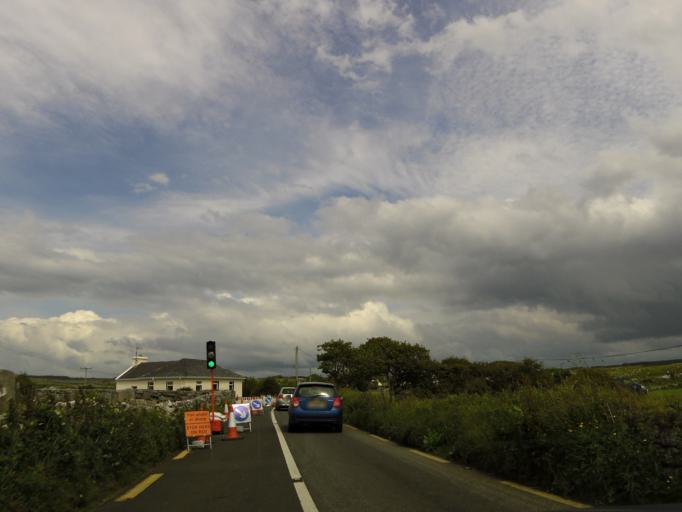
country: IE
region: Connaught
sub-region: County Galway
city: Bearna
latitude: 53.0440
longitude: -9.2547
